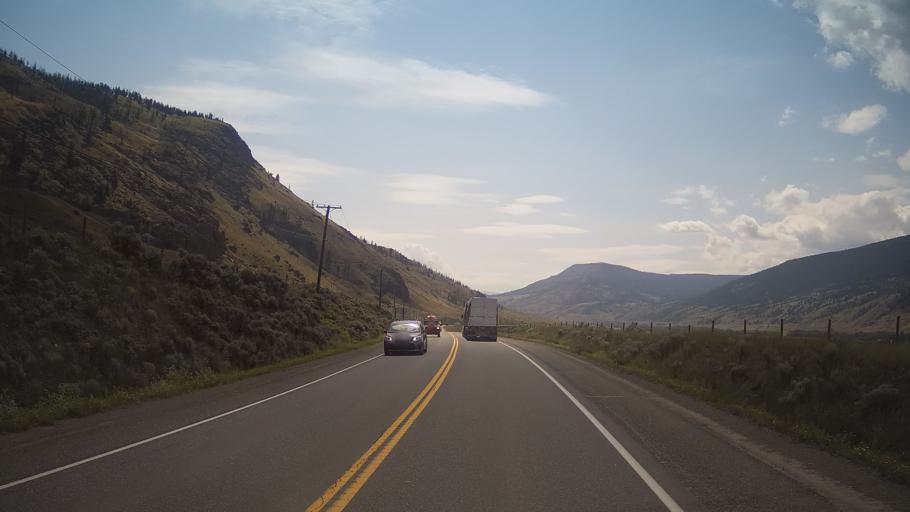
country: CA
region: British Columbia
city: Cache Creek
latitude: 50.8841
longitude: -121.3988
